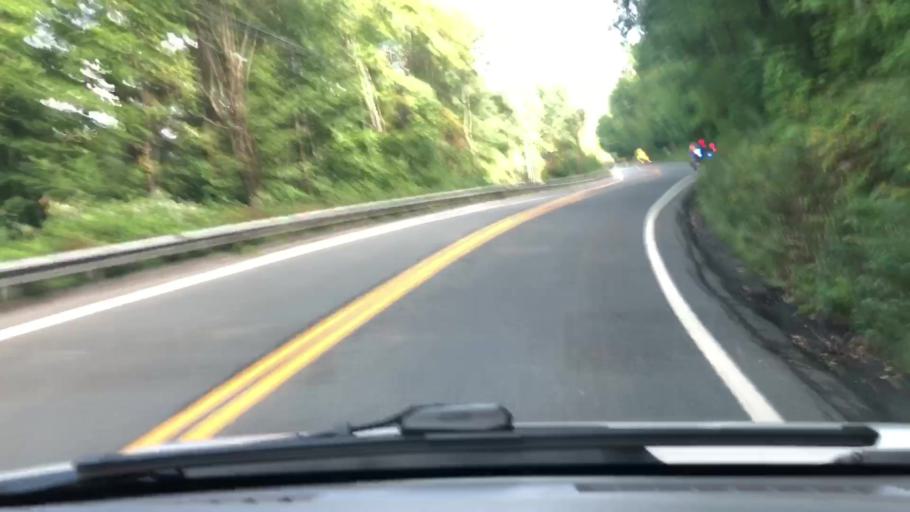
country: US
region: Massachusetts
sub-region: Berkshire County
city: North Adams
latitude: 42.6975
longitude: -73.0730
